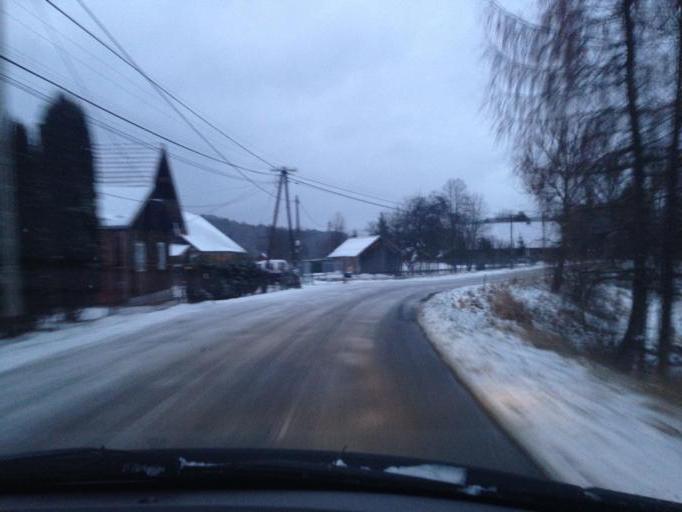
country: PL
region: Subcarpathian Voivodeship
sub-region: Powiat jasielski
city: Krempna
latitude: 49.5102
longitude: 21.5076
